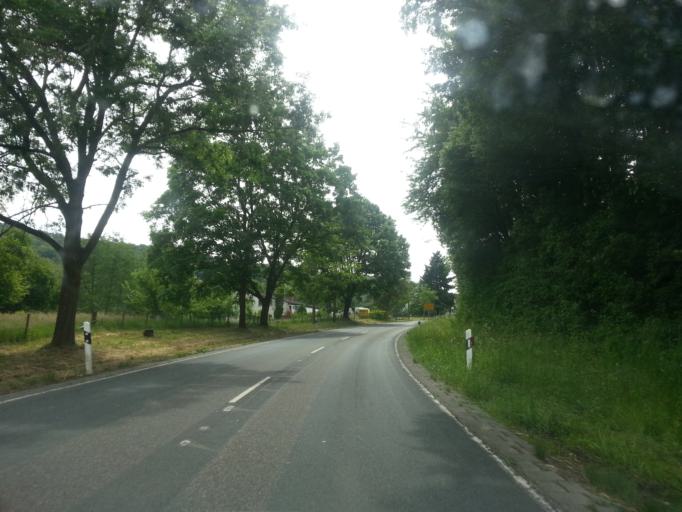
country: DE
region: Hesse
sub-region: Regierungsbezirk Darmstadt
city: Seeheim-Jugenheim
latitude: 49.7398
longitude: 8.6555
